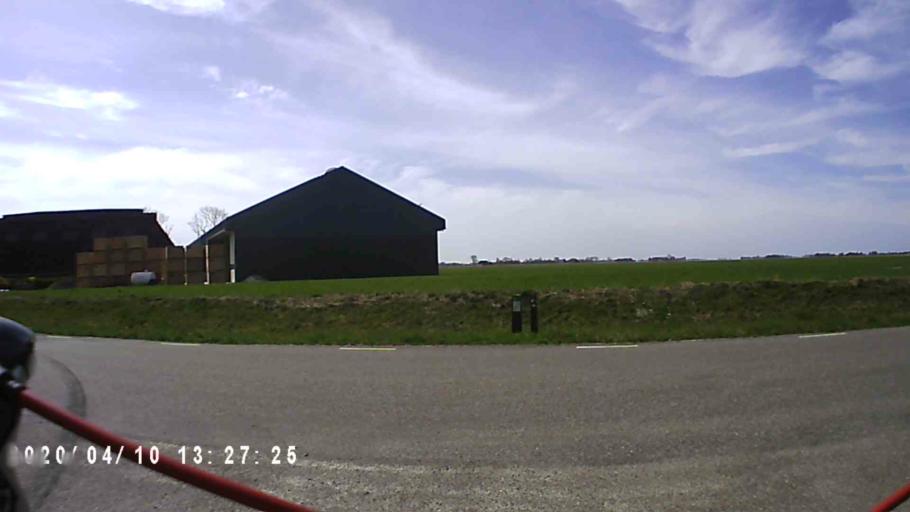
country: NL
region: Groningen
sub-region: Gemeente Zuidhorn
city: Oldehove
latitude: 53.3796
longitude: 6.4212
